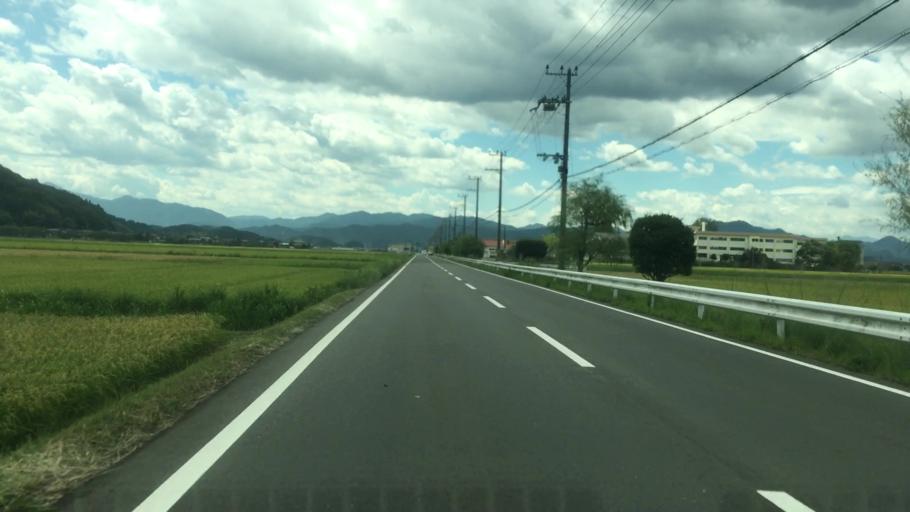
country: JP
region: Hyogo
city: Toyooka
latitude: 35.5337
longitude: 134.8397
